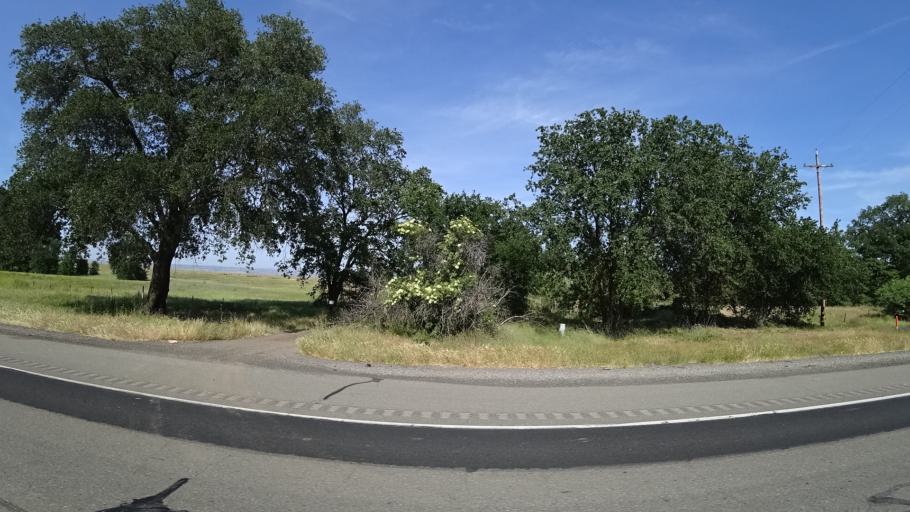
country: US
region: California
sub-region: Tehama County
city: Los Molinos
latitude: 39.9488
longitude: -122.0547
